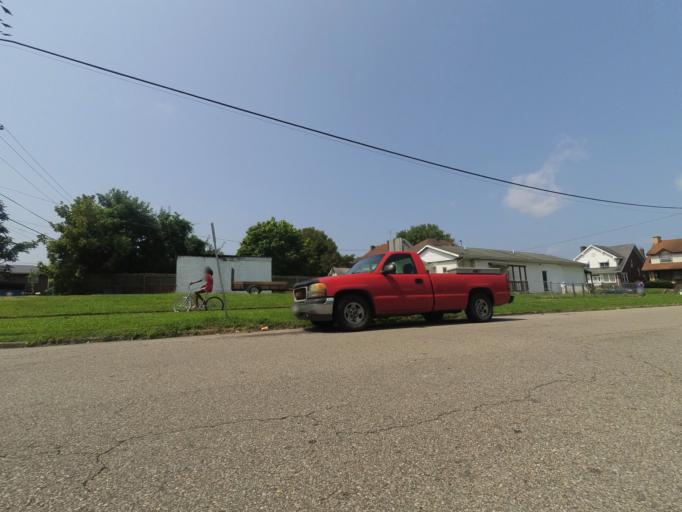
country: US
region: West Virginia
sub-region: Cabell County
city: Huntington
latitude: 38.4281
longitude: -82.4132
